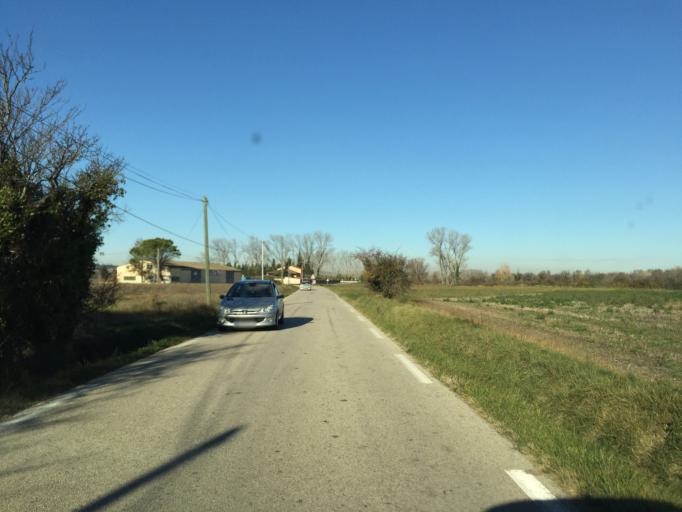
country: FR
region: Provence-Alpes-Cote d'Azur
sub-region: Departement du Vaucluse
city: Entraigues-sur-la-Sorgue
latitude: 44.0182
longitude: 4.9280
